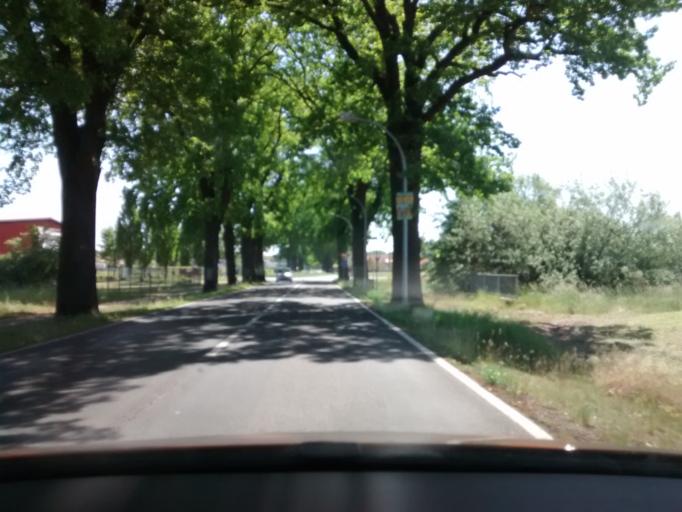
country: DE
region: Brandenburg
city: Storkow
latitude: 52.2658
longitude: 13.9315
